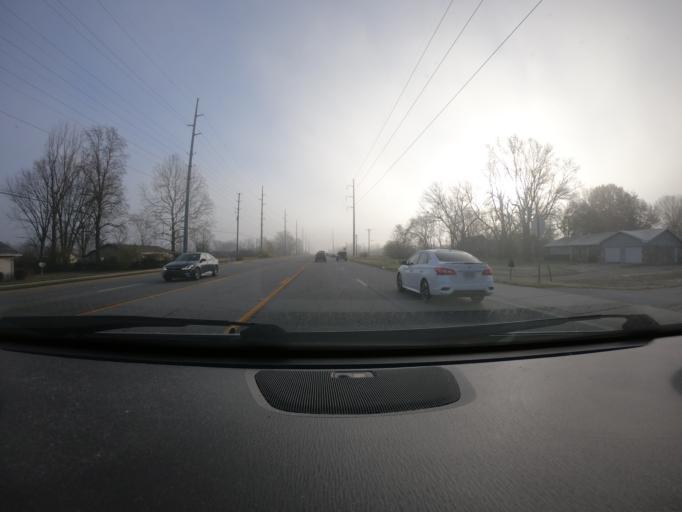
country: US
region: Arkansas
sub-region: Benton County
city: Bentonville
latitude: 36.3574
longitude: -94.2356
